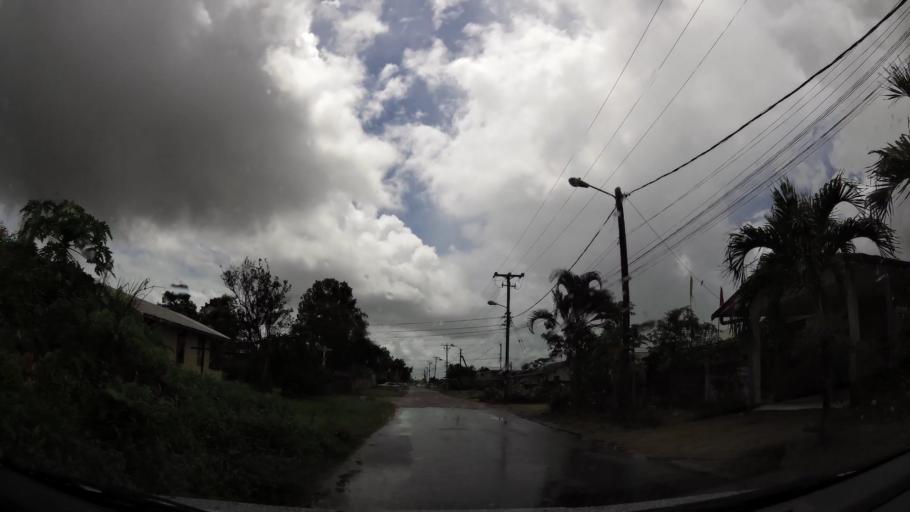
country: SR
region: Paramaribo
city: Paramaribo
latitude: 5.8288
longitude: -55.2316
